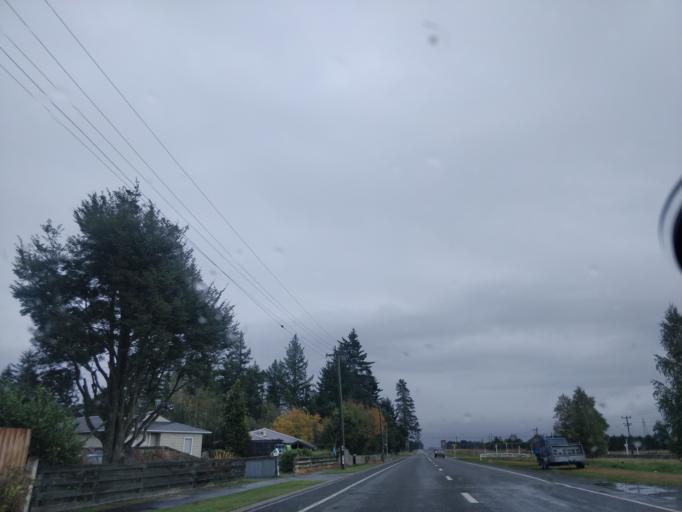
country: NZ
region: Canterbury
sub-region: Selwyn District
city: Darfield
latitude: -43.3866
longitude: 172.0156
